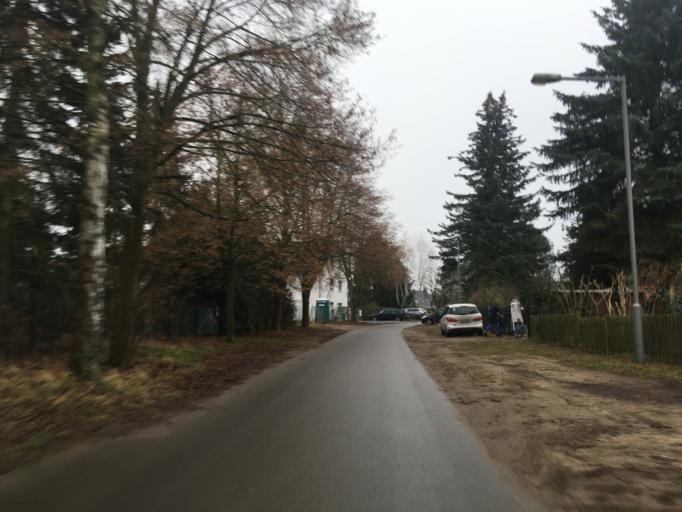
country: DE
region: Berlin
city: Buch
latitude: 52.6364
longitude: 13.5192
